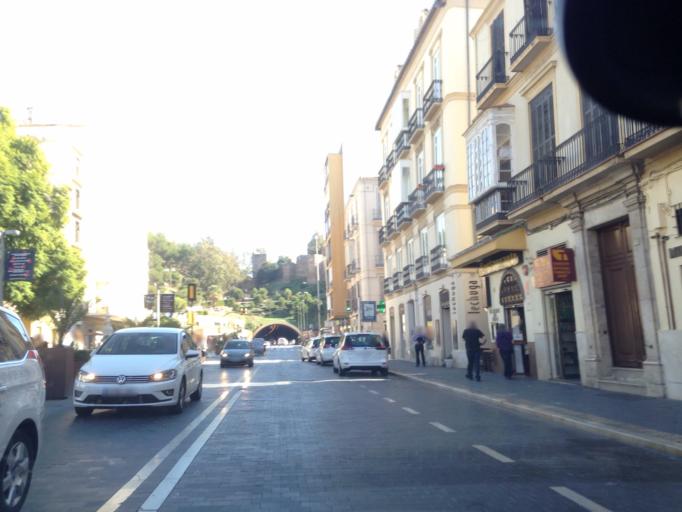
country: ES
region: Andalusia
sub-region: Provincia de Malaga
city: Malaga
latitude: 36.7231
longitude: -4.4181
